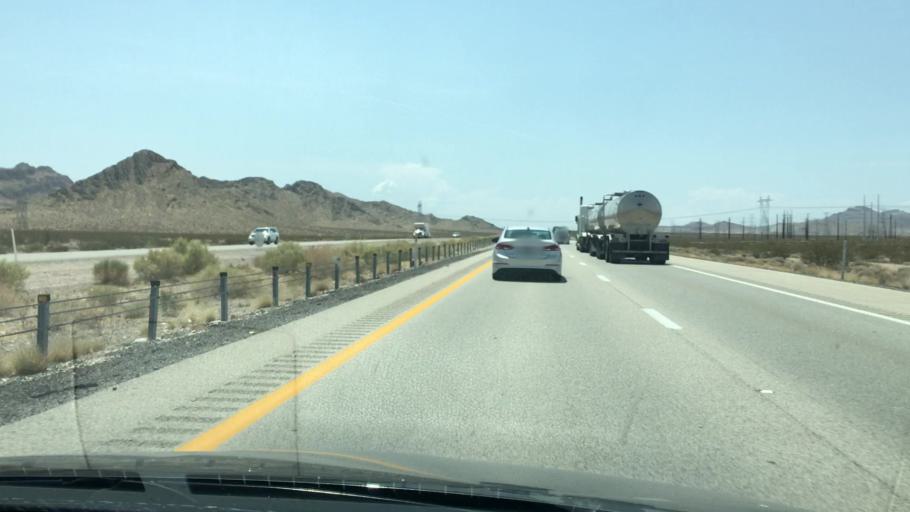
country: US
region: Nevada
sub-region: Clark County
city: Nellis Air Force Base
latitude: 36.4118
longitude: -114.8730
